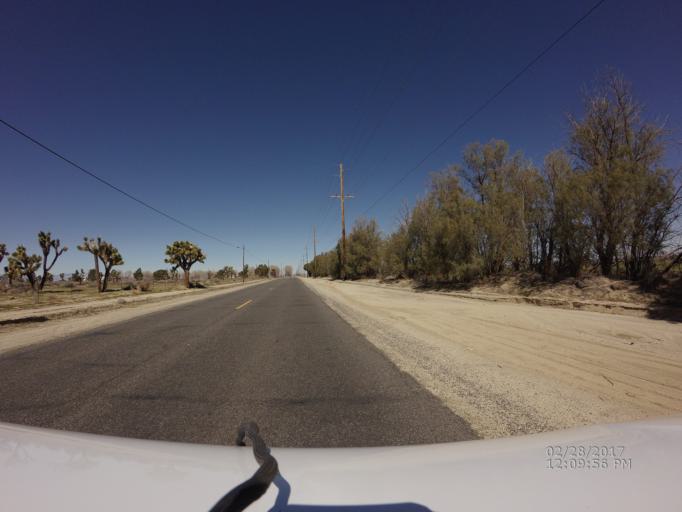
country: US
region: California
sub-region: Los Angeles County
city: Palmdale
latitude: 34.5930
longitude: -118.0585
